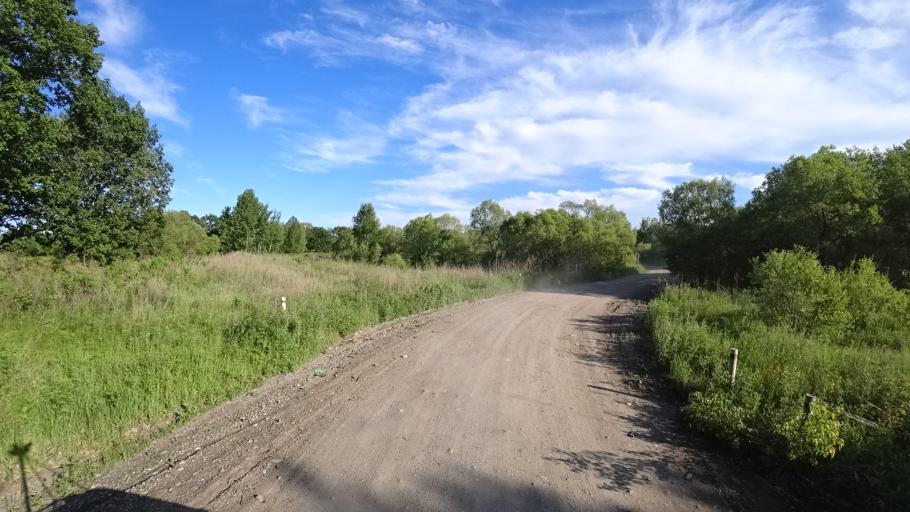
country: RU
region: Khabarovsk Krai
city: Khor
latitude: 47.8529
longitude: 134.9445
